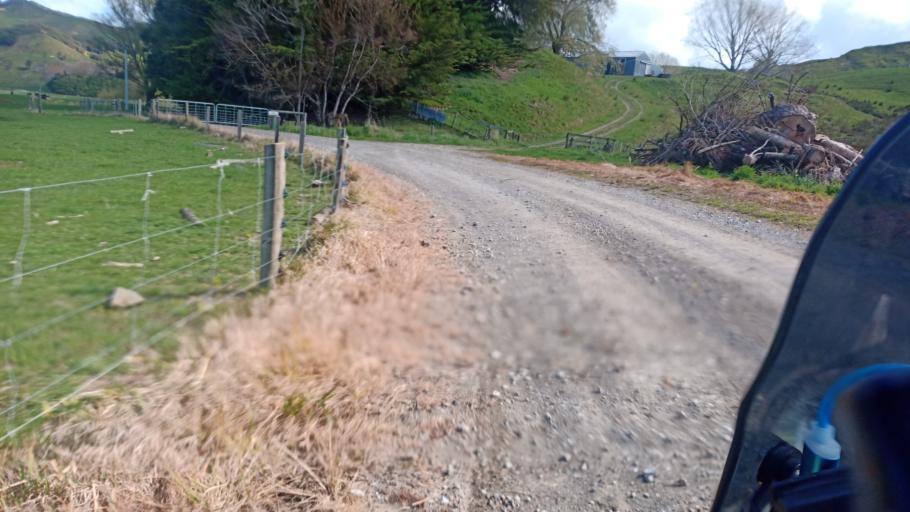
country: NZ
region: Gisborne
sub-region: Gisborne District
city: Gisborne
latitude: -38.3869
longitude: 178.2604
